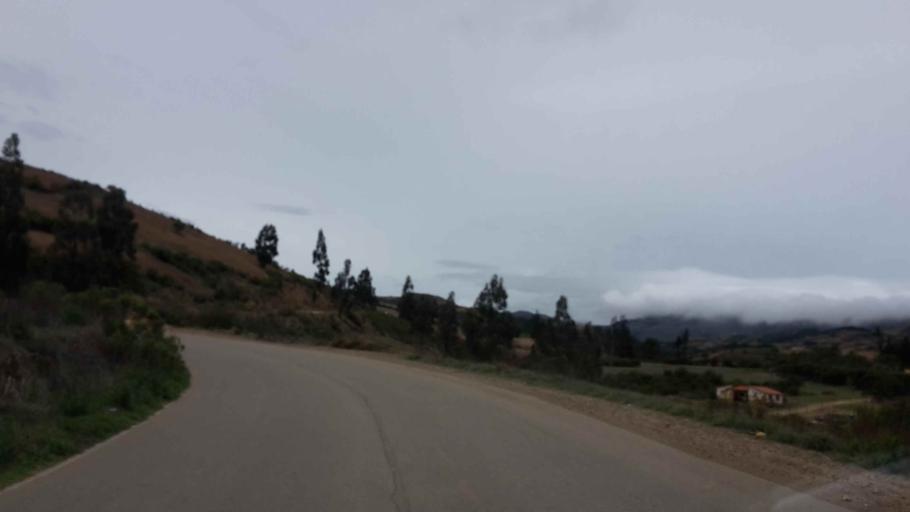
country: BO
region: Cochabamba
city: Totora
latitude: -17.7044
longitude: -65.2123
